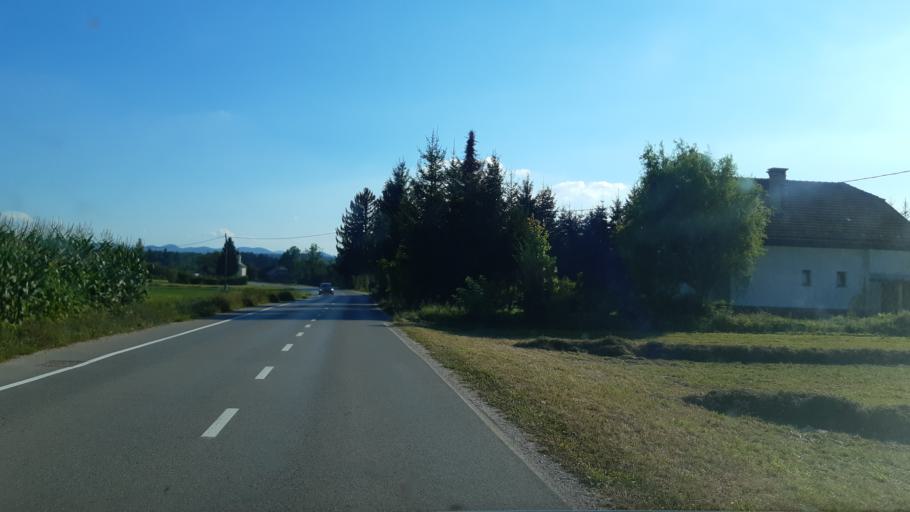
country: SI
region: Ivancna Gorica
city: Ivancna Gorica
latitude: 45.9511
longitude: 14.8038
